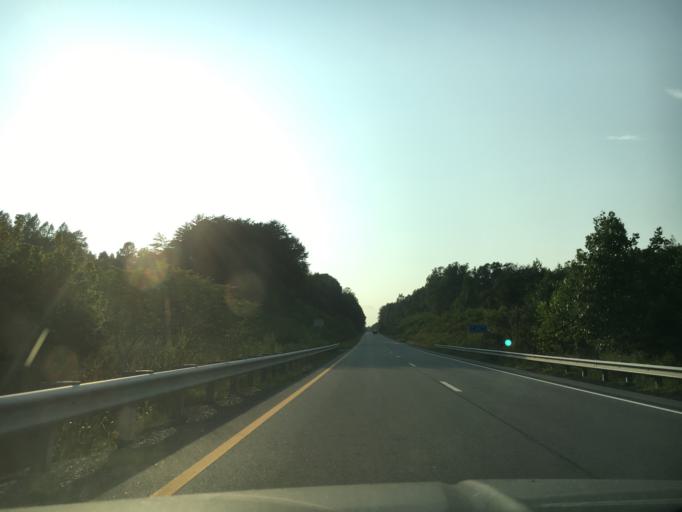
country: US
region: Virginia
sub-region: Appomattox County
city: Appomattox
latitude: 37.2710
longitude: -78.6705
